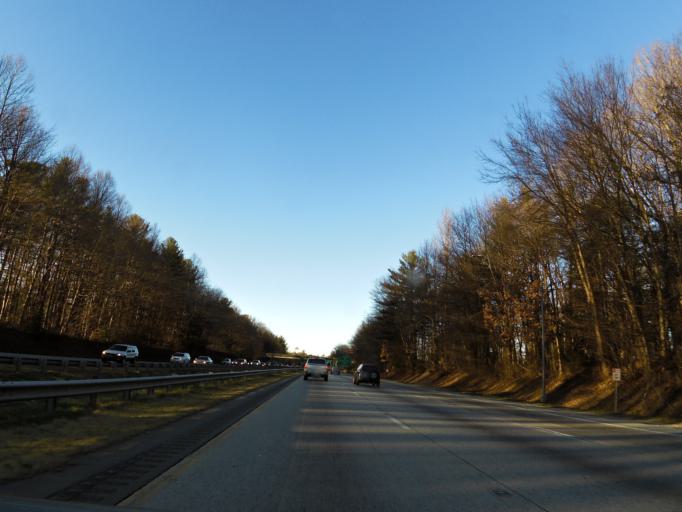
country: US
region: North Carolina
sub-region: Henderson County
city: Fletcher
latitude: 35.4297
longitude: -82.5297
